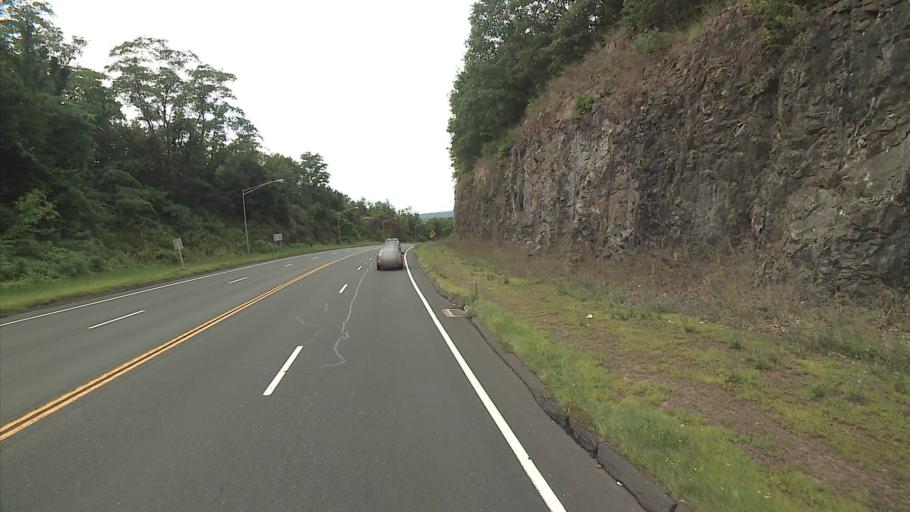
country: US
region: Connecticut
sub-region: Hartford County
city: Newington
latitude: 41.6979
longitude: -72.7097
